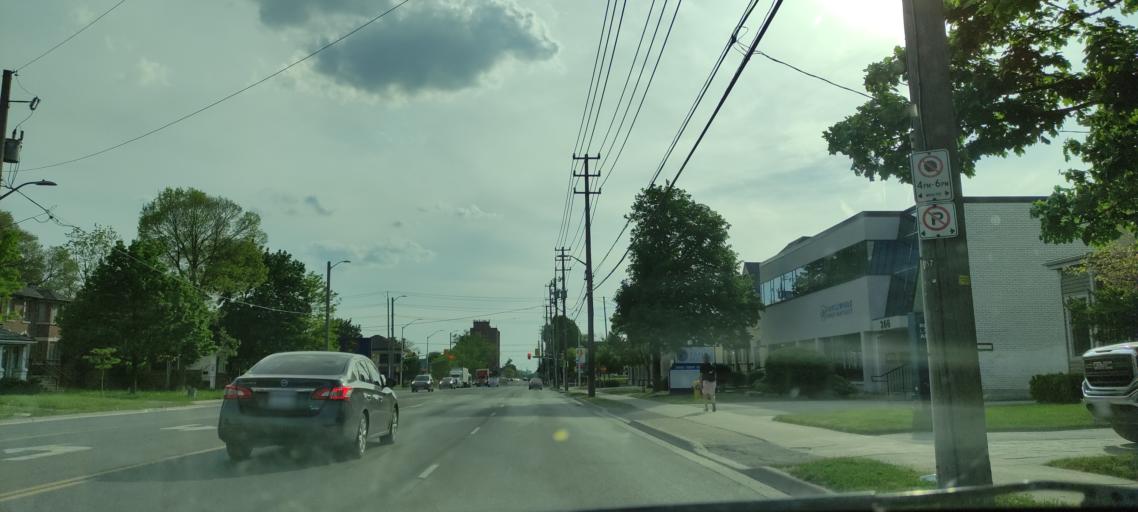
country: CA
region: Ontario
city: London
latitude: 42.9975
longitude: -81.2466
